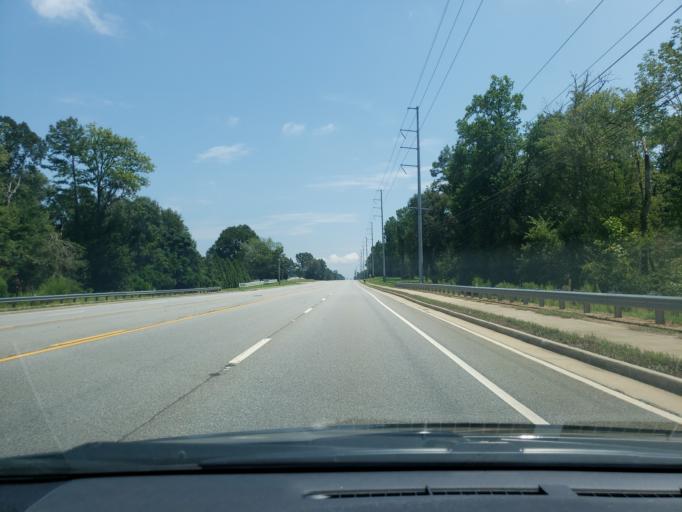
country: US
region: Georgia
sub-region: Dougherty County
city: Albany
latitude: 31.5856
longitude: -84.2646
